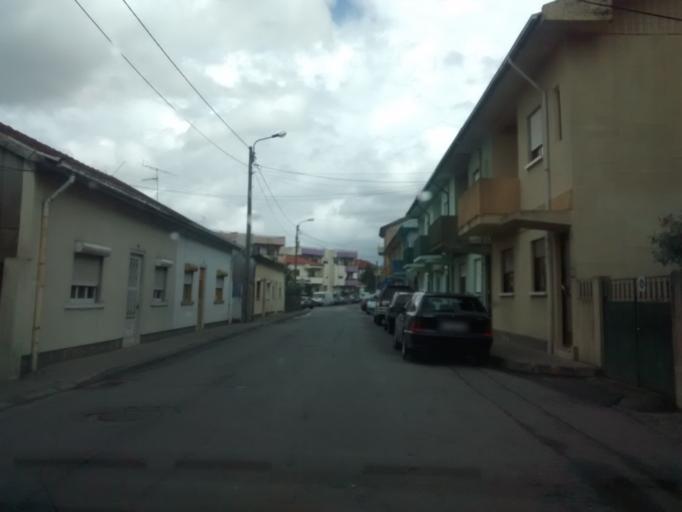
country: PT
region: Braga
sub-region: Braga
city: Braga
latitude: 41.5406
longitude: -8.4384
